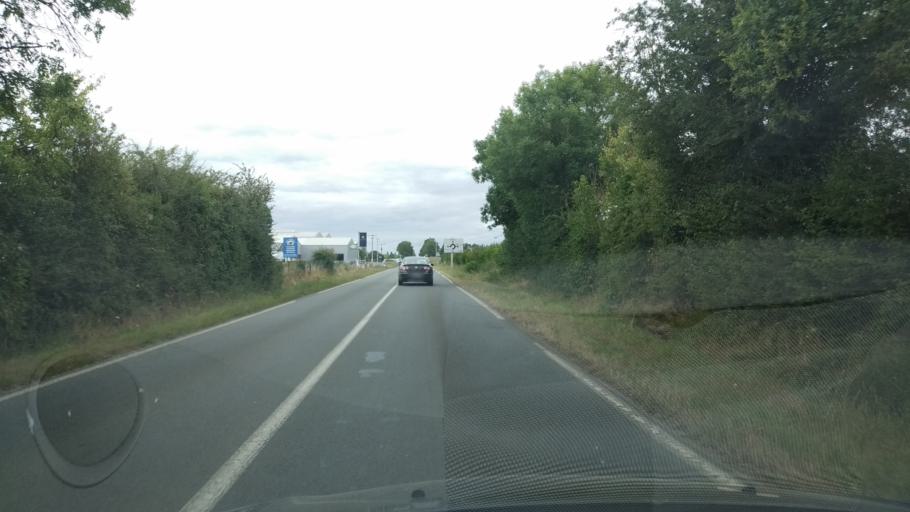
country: FR
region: Poitou-Charentes
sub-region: Departement de la Vienne
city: Roches-Premarie-Andille
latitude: 46.4924
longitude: 0.3670
